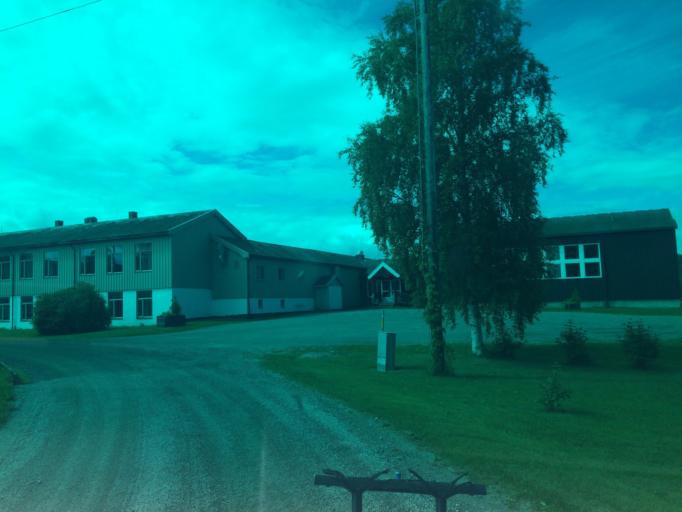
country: NO
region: Nord-Trondelag
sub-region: Overhalla
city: Ranemsletta
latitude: 64.4648
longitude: 12.0564
